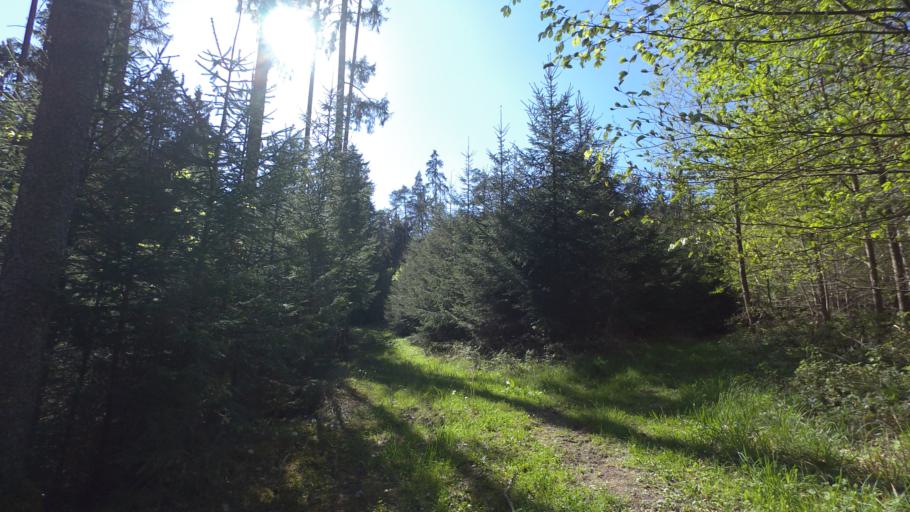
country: DE
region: Bavaria
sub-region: Upper Bavaria
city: Chieming
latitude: 47.9478
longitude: 12.5341
